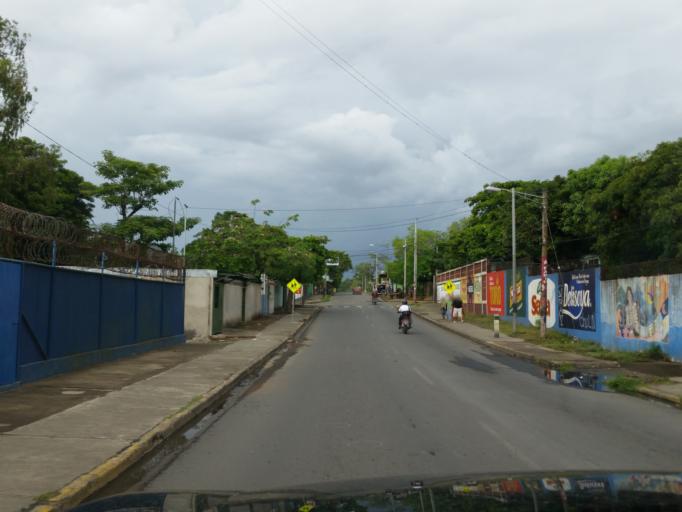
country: NI
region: Managua
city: Managua
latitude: 12.1074
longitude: -86.2975
